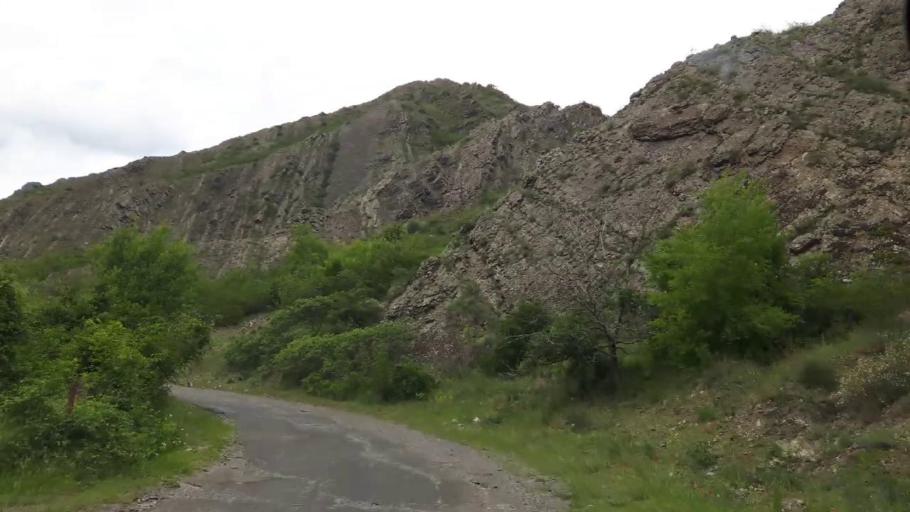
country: GE
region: Shida Kartli
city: Gori
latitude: 41.9006
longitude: 44.0847
